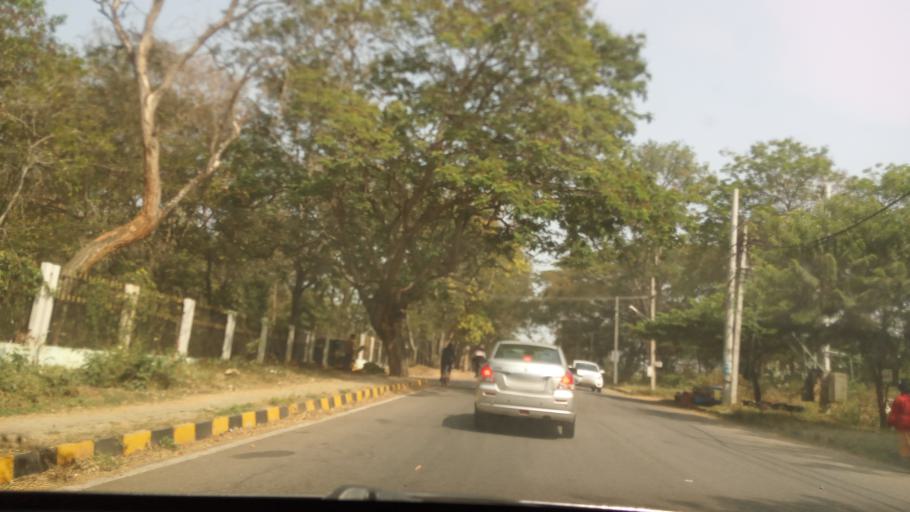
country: IN
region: Karnataka
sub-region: Mysore
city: Mysore
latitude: 12.3102
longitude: 76.6265
